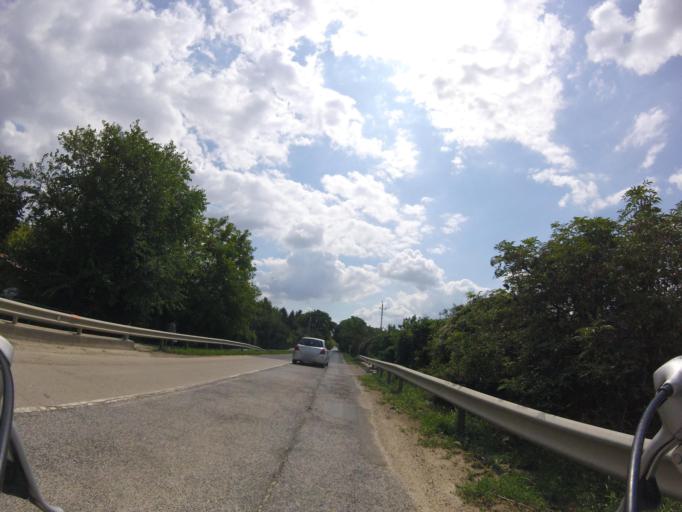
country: HU
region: Pest
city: Soskut
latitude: 47.4244
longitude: 18.8259
